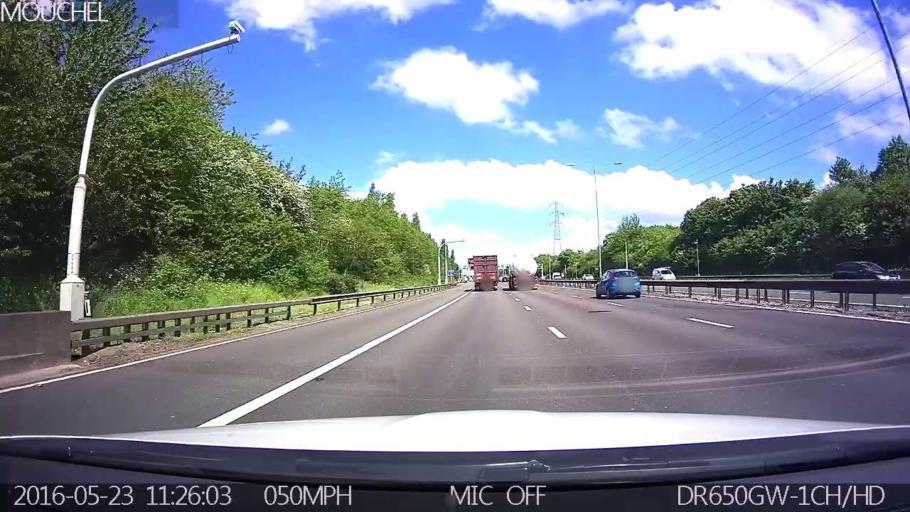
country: GB
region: England
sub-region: Walsall
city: Bloxwich
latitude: 52.5997
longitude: -2.0163
